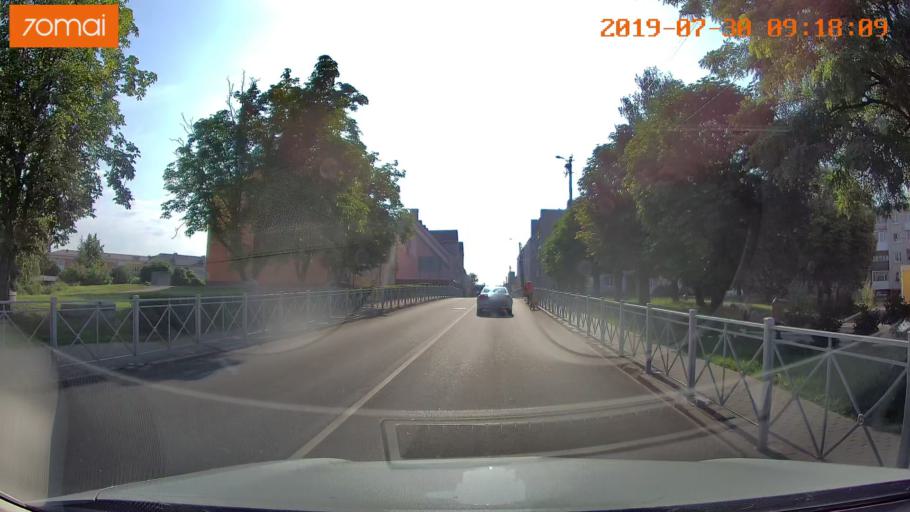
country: RU
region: Kaliningrad
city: Nesterov
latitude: 54.6310
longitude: 22.5729
